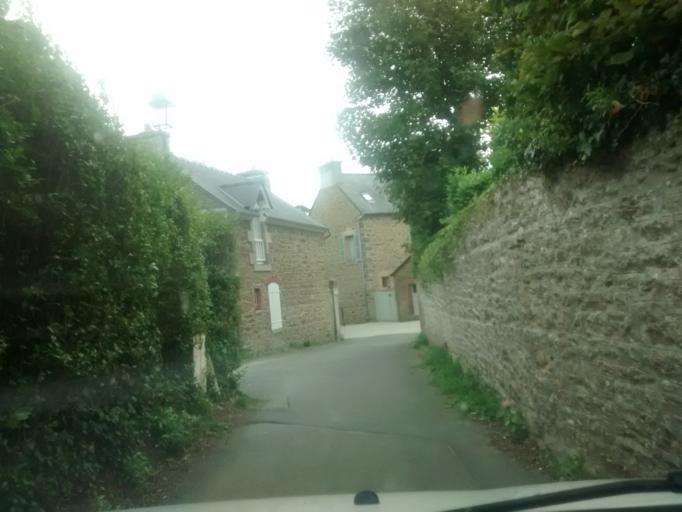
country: FR
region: Brittany
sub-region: Departement d'Ille-et-Vilaine
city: Saint-Briac-sur-Mer
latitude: 48.6214
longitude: -2.1342
